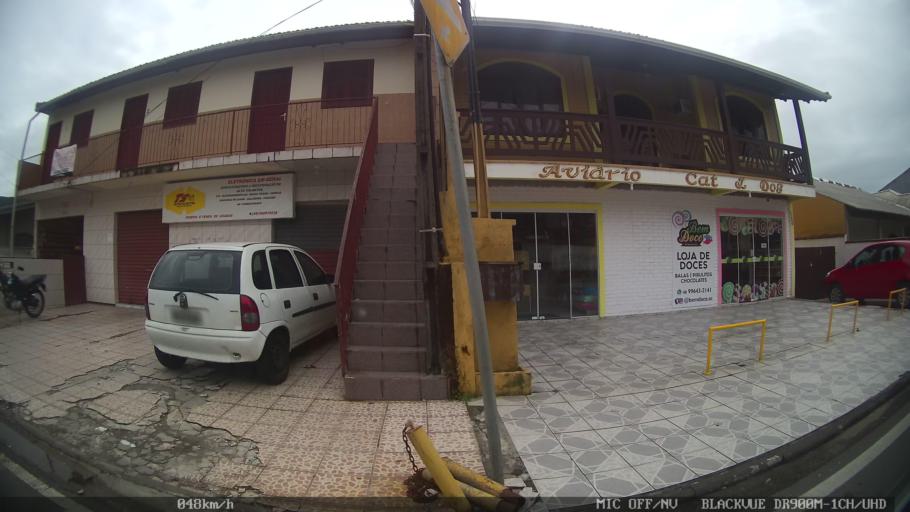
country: BR
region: Santa Catarina
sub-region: Biguacu
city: Biguacu
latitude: -27.5435
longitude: -48.6386
